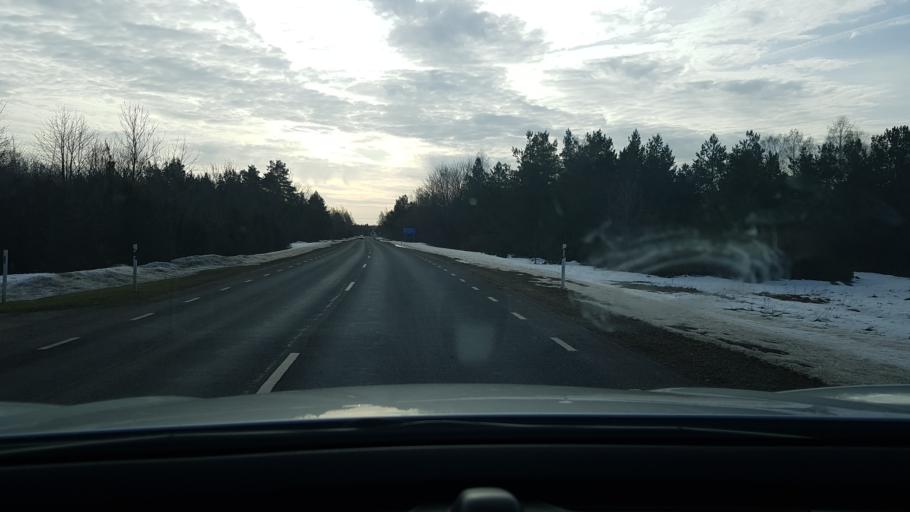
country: EE
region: Saare
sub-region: Kuressaare linn
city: Kuressaare
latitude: 58.2866
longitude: 22.5399
